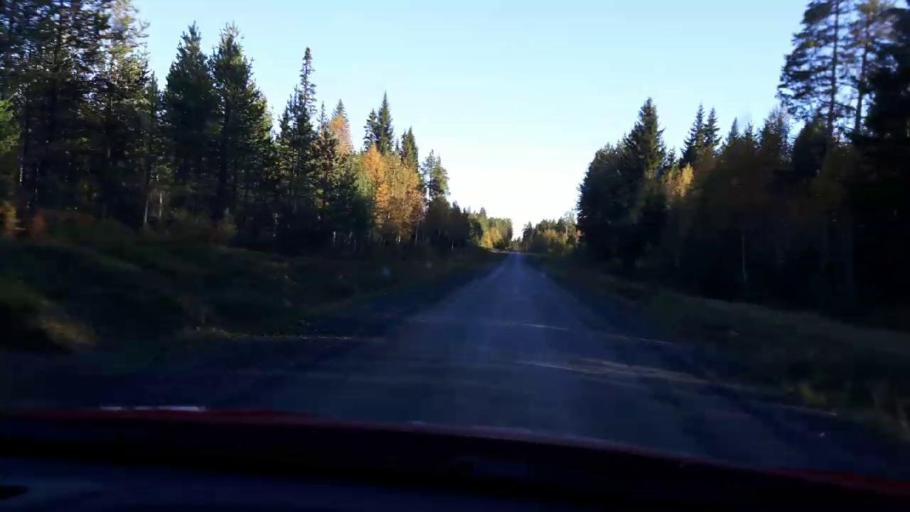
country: SE
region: Jaemtland
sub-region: OEstersunds Kommun
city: Lit
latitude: 63.6471
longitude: 14.7197
